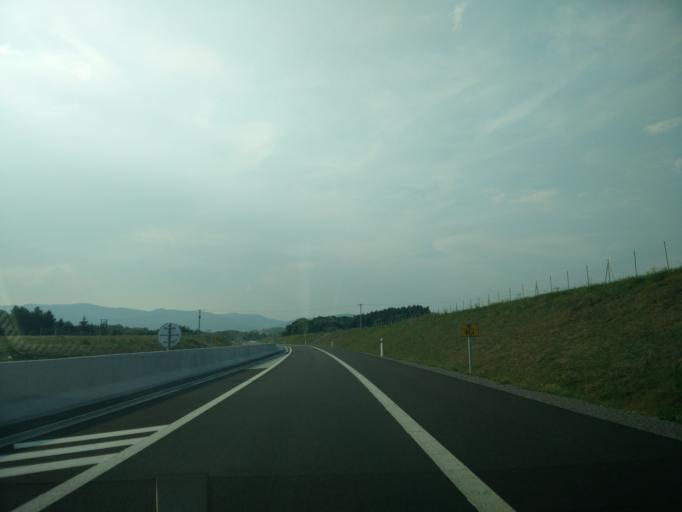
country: SK
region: Banskobystricky
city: Ziar nad Hronom
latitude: 48.5893
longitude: 18.8315
